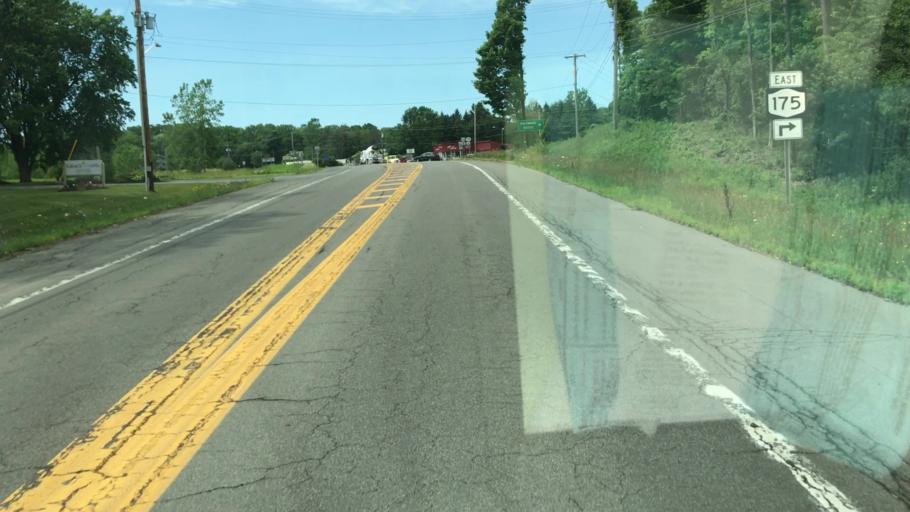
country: US
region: New York
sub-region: Onondaga County
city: Skaneateles
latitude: 42.9445
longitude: -76.3911
